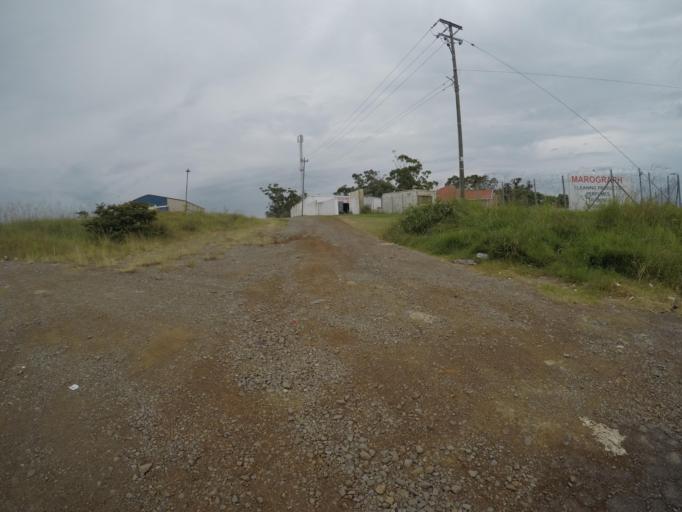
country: ZA
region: Eastern Cape
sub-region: Buffalo City Metropolitan Municipality
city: East London
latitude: -32.9679
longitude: 27.8489
